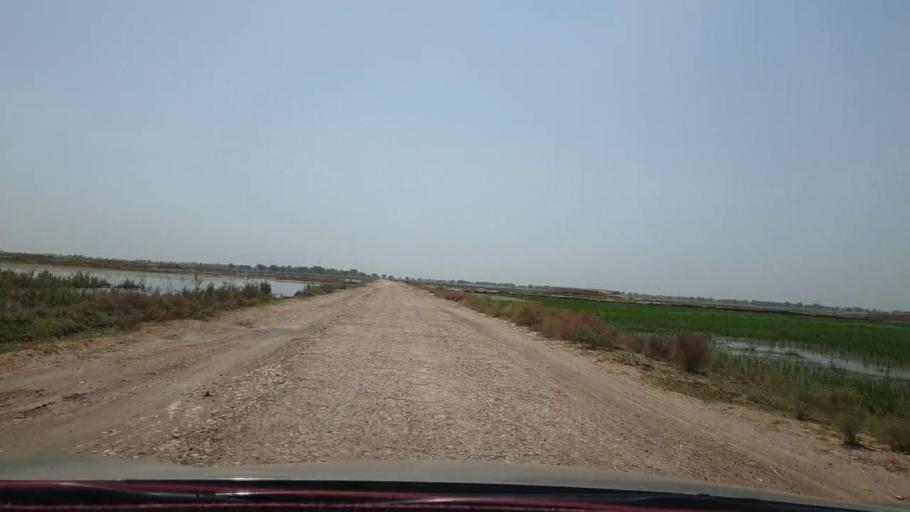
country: PK
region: Sindh
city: Kambar
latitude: 27.5804
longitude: 67.8776
